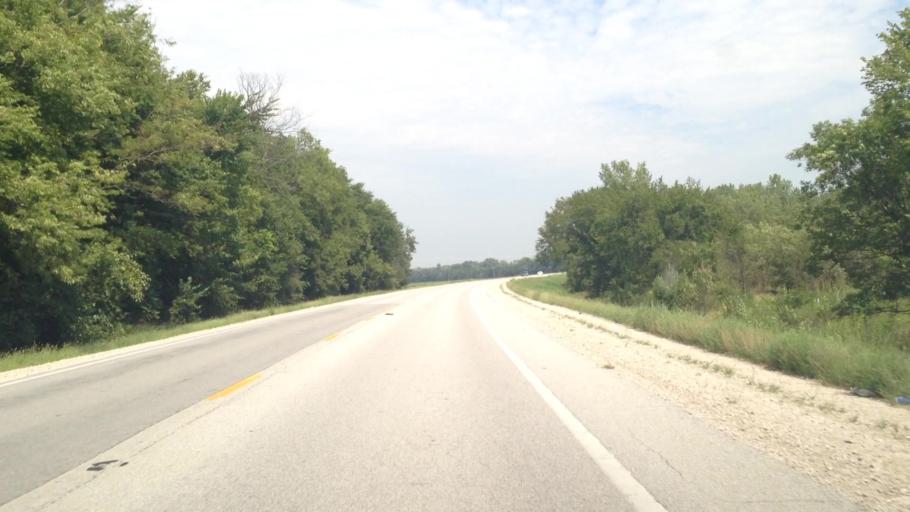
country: US
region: Kansas
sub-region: Neosho County
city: Erie
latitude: 37.5409
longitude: -95.2696
